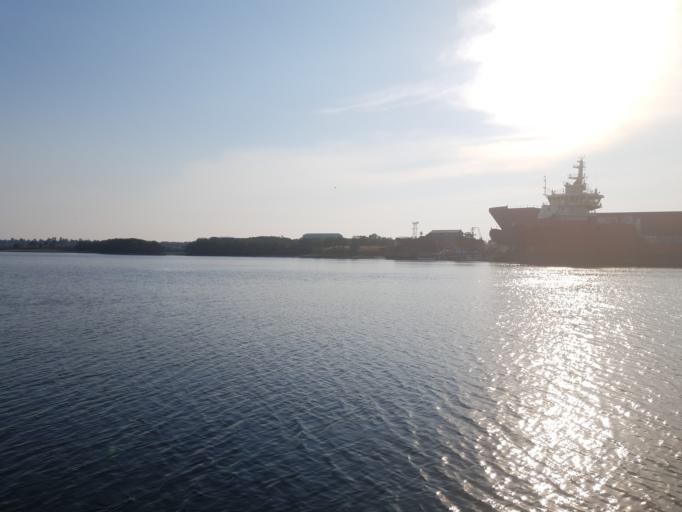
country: IN
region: Karnataka
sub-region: Dakshina Kannada
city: Mangalore
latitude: 12.8748
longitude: 74.8255
